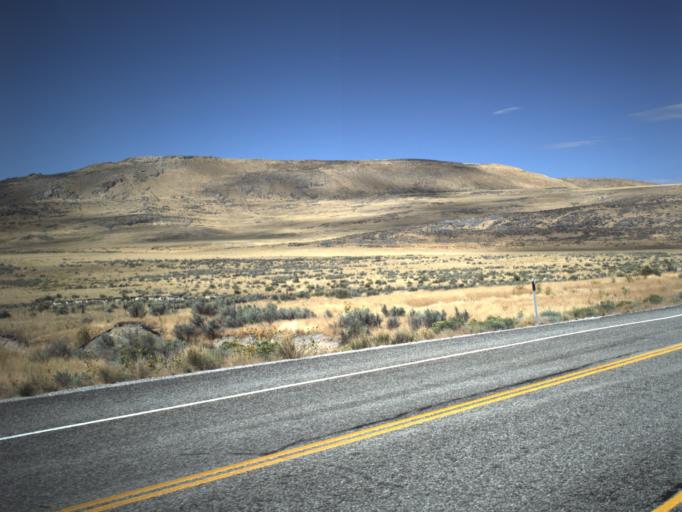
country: US
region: Utah
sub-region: Box Elder County
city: Tremonton
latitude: 41.6636
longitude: -112.4439
